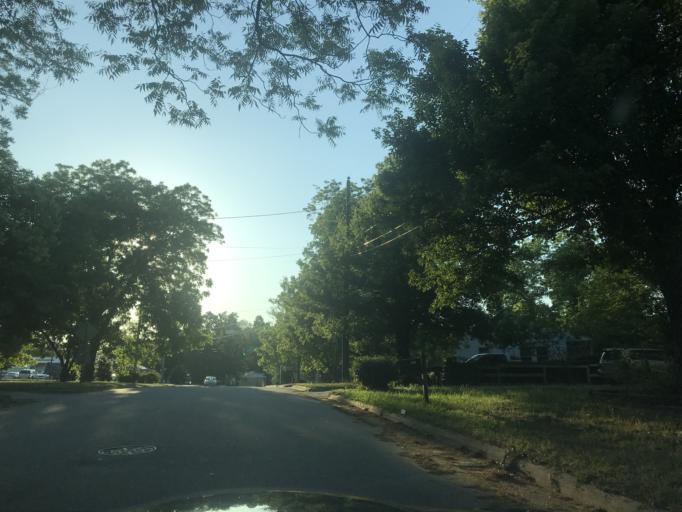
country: US
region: North Carolina
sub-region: Wake County
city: Raleigh
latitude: 35.7479
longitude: -78.6429
